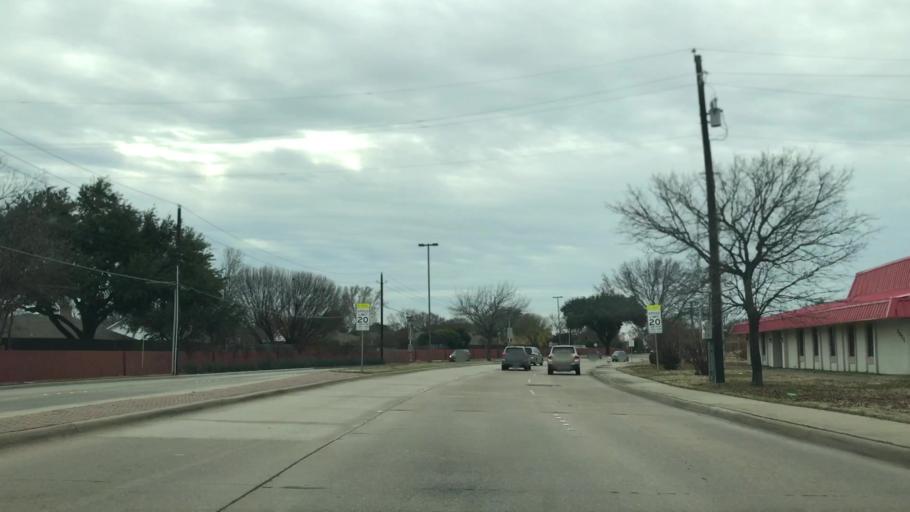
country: US
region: Texas
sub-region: Dallas County
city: Carrollton
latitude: 33.0192
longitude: -96.8851
